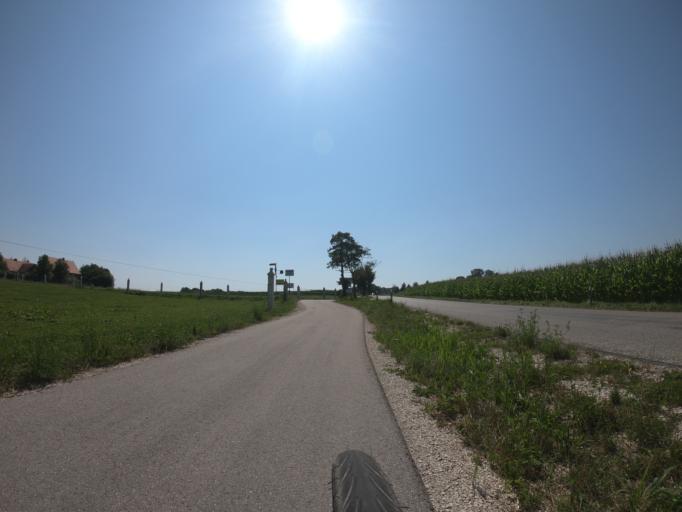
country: DE
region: Bavaria
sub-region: Upper Bavaria
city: Fuerstenfeldbruck
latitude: 48.1578
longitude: 11.2584
